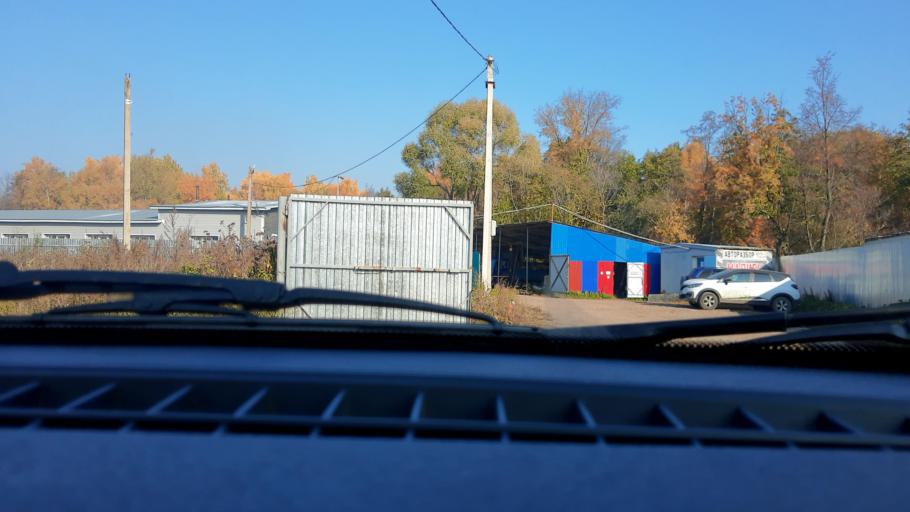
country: RU
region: Bashkortostan
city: Mikhaylovka
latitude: 54.8068
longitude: 55.8263
